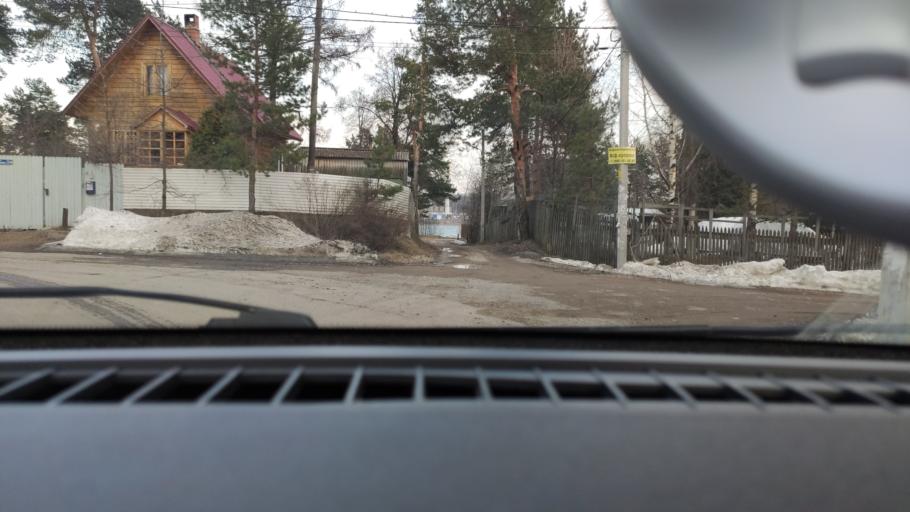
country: RU
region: Perm
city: Perm
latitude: 58.0532
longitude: 56.2987
